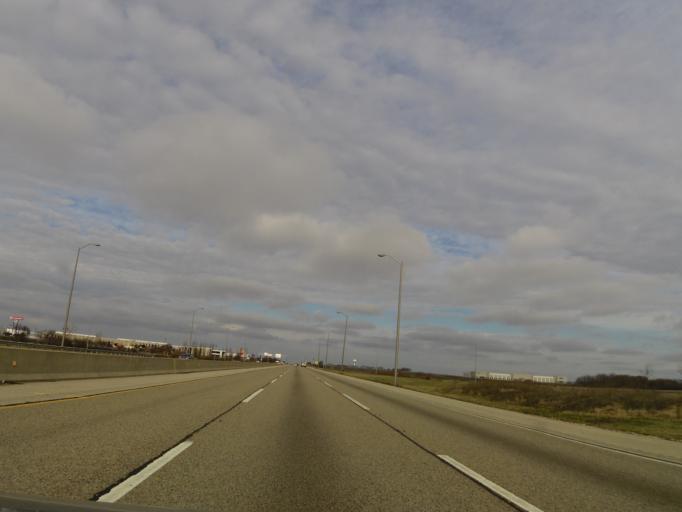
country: US
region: Illinois
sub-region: Winnebago County
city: Machesney Park
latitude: 42.3193
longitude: -88.9646
